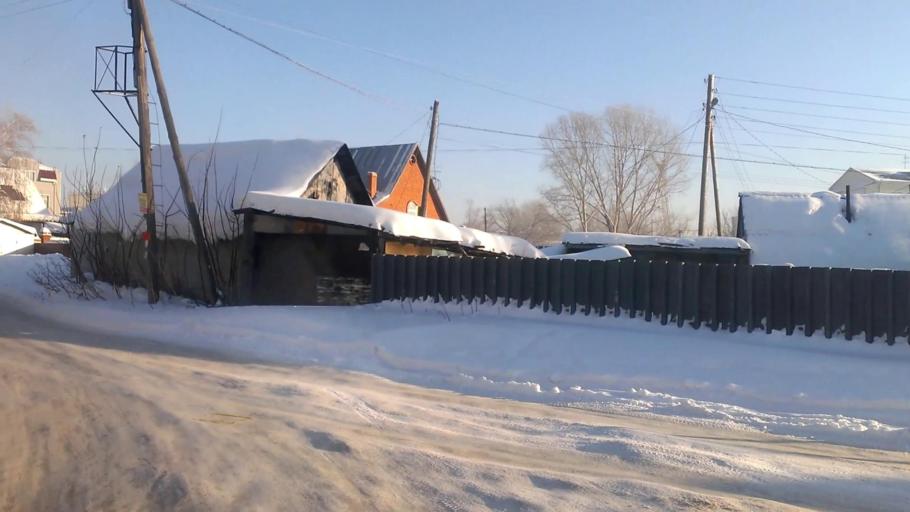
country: RU
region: Altai Krai
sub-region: Gorod Barnaulskiy
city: Barnaul
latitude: 53.3477
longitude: 83.7267
